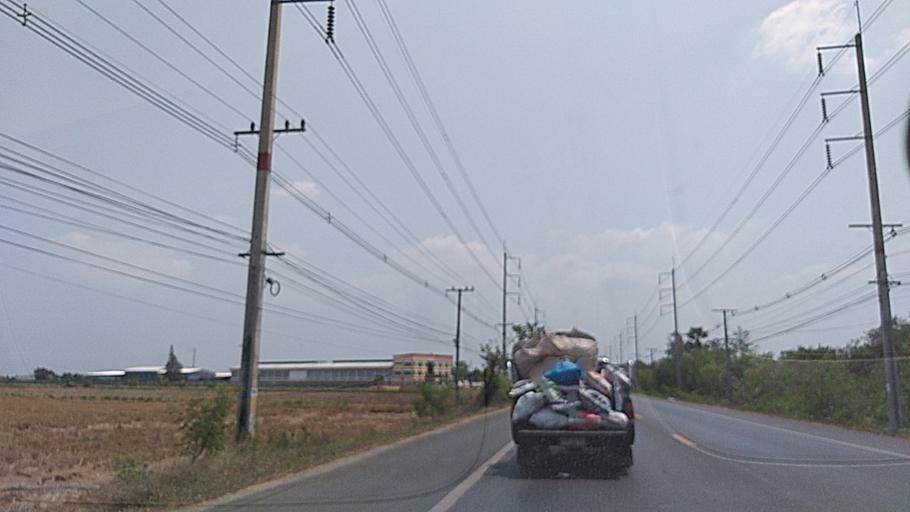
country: TH
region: Chachoengsao
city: Bang Nam Priao
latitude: 13.7830
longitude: 101.0594
